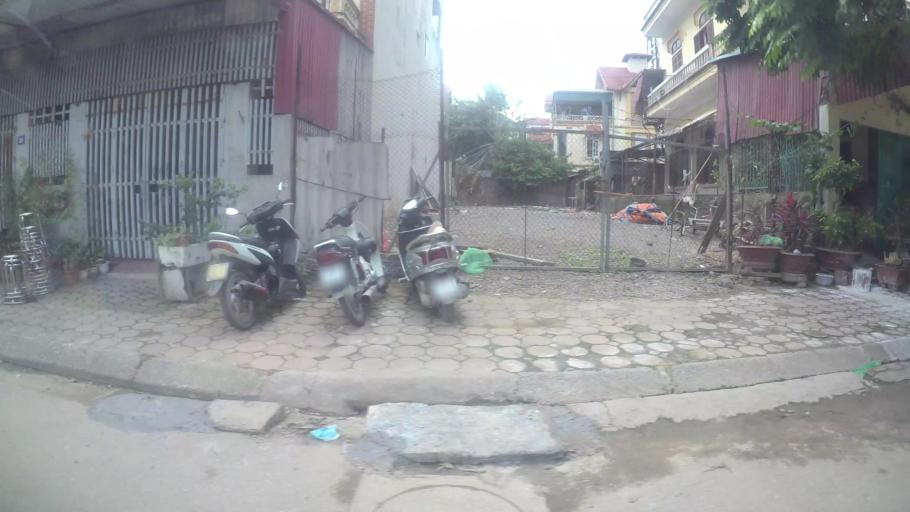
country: VN
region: Ha Noi
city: Tay Ho
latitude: 21.0883
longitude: 105.7956
